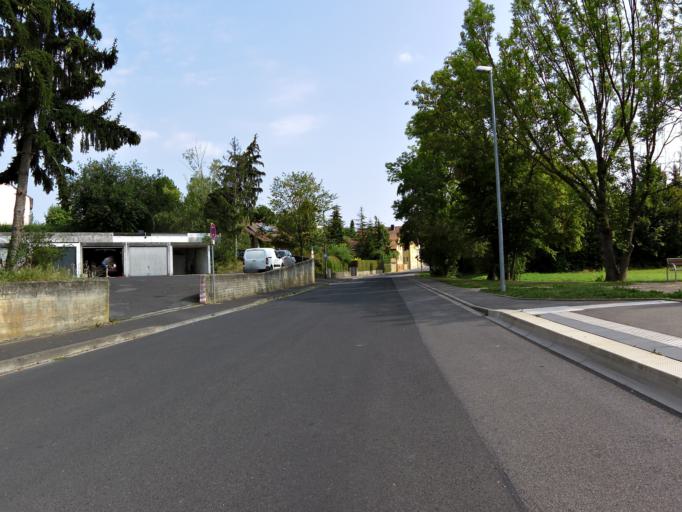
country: DE
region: Bavaria
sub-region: Regierungsbezirk Unterfranken
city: Estenfeld
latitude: 49.8246
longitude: 10.0070
